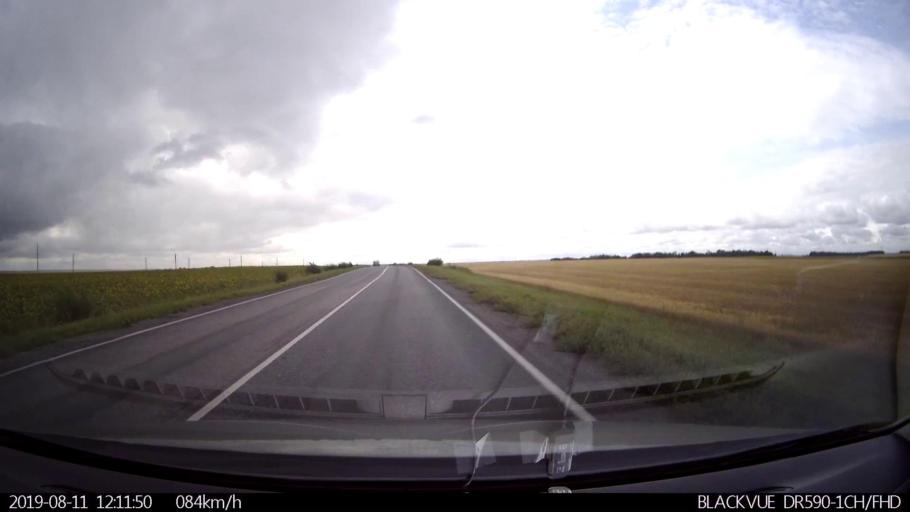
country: RU
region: Ulyanovsk
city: Silikatnyy
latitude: 53.9809
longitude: 48.0001
